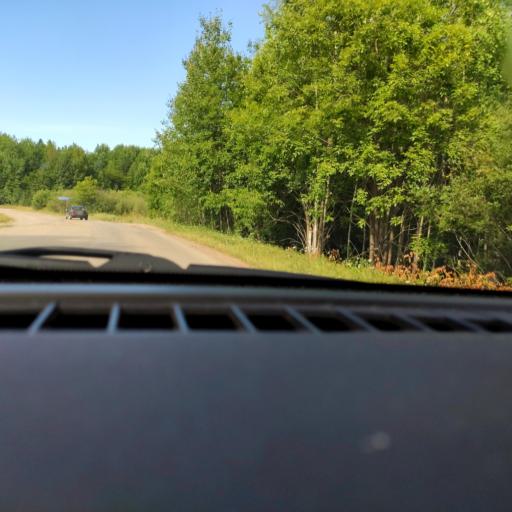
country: RU
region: Perm
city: Polazna
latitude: 58.3605
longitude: 56.2483
